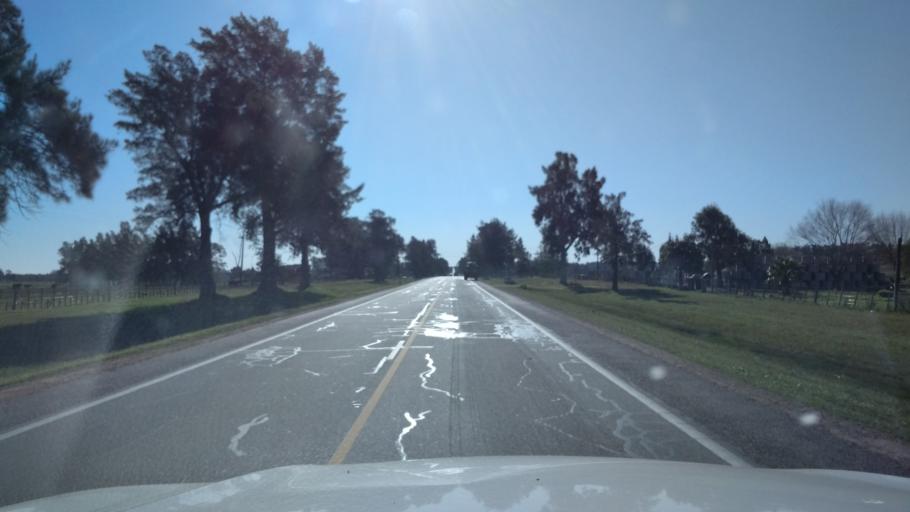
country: UY
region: Canelones
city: San Jacinto
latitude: -34.5854
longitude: -55.8403
